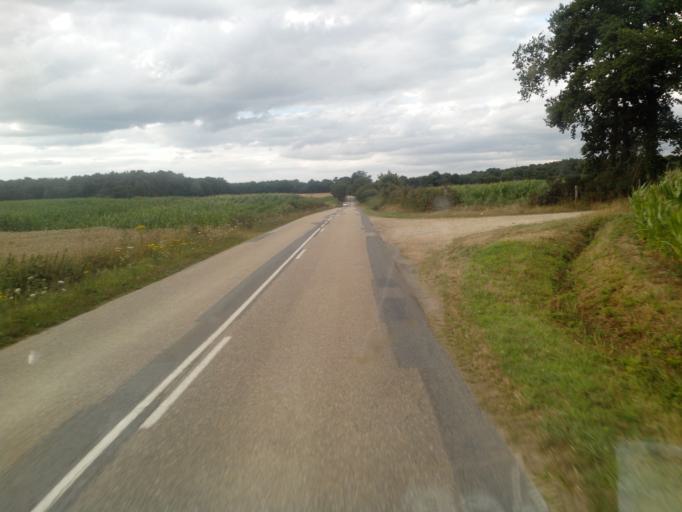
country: FR
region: Brittany
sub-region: Departement d'Ille-et-Vilaine
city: Maxent
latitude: 47.9490
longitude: -2.0093
